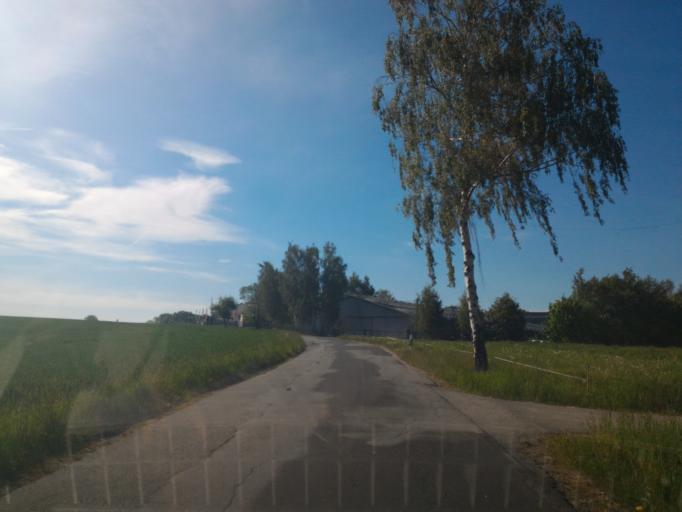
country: DE
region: Saxony
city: Grossschweidnitz
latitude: 51.0574
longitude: 14.6375
